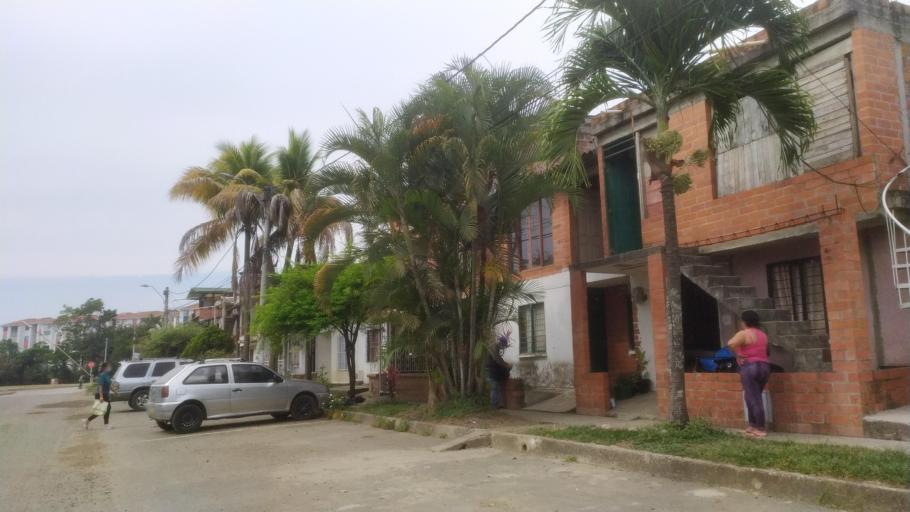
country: CO
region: Valle del Cauca
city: Jamundi
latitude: 3.2375
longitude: -76.5066
